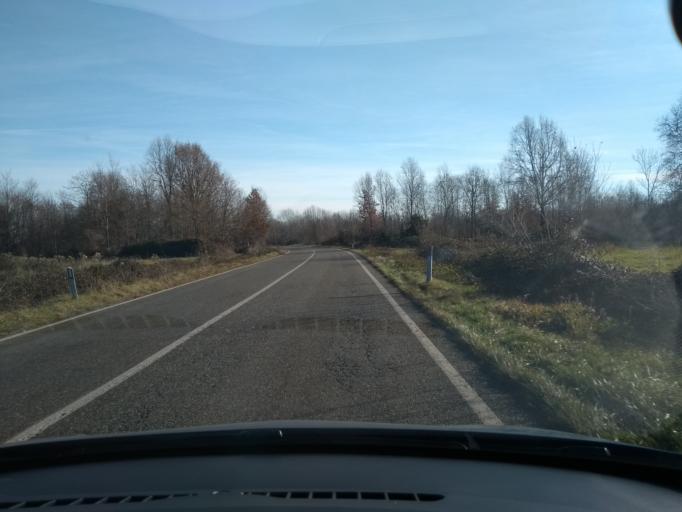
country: IT
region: Piedmont
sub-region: Provincia di Torino
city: Vauda Canavese Superiore
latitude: 45.2797
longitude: 7.6019
